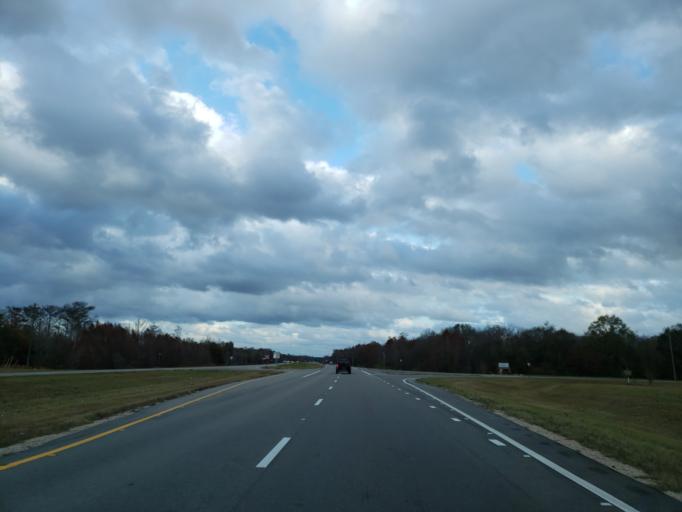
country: US
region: Mississippi
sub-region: Perry County
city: New Augusta
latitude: 31.1202
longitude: -88.8387
